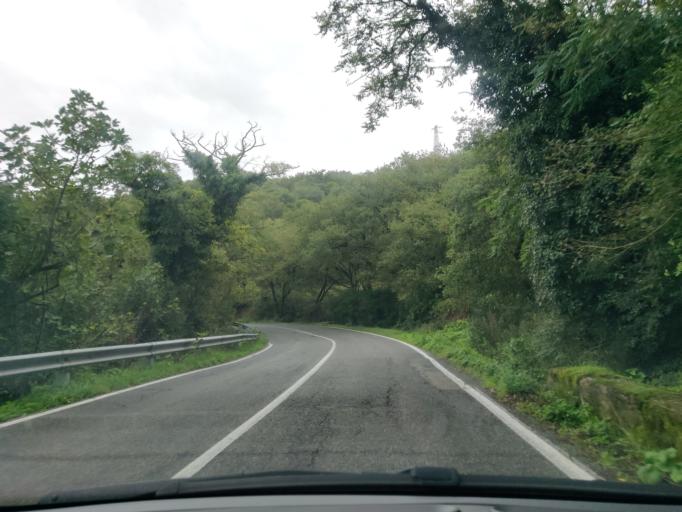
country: IT
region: Latium
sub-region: Citta metropolitana di Roma Capitale
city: Allumiere
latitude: 42.1455
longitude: 11.8958
